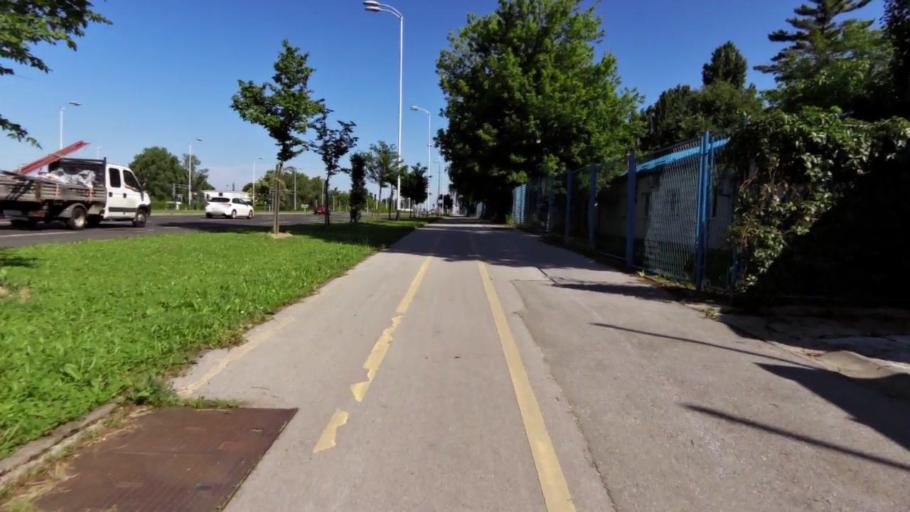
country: HR
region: Grad Zagreb
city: Novi Zagreb
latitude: 45.7911
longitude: 16.0289
